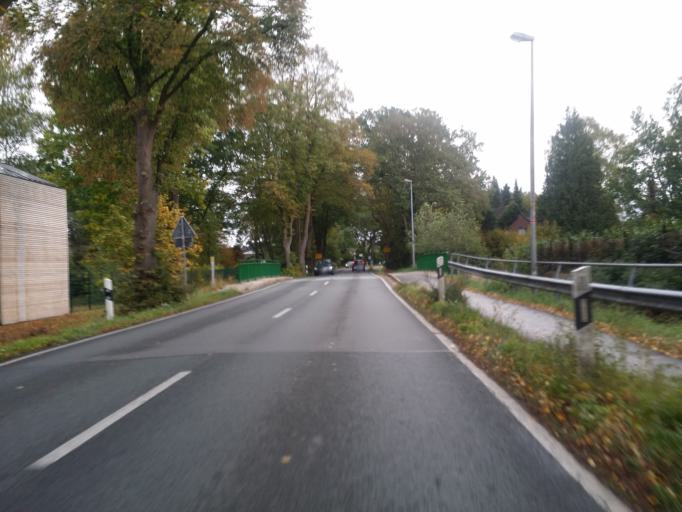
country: DE
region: Lower Saxony
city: Stuhr
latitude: 53.0388
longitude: 8.7179
